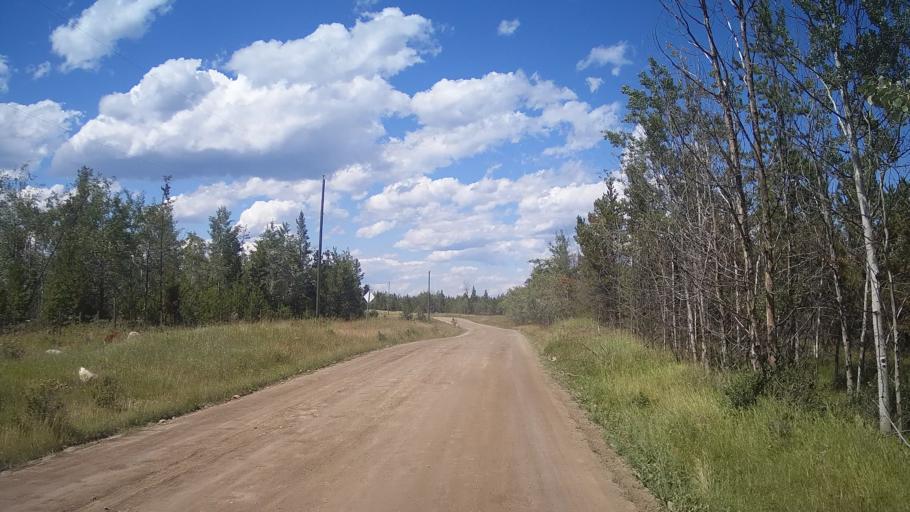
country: CA
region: British Columbia
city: Cache Creek
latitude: 51.2656
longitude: -121.6996
